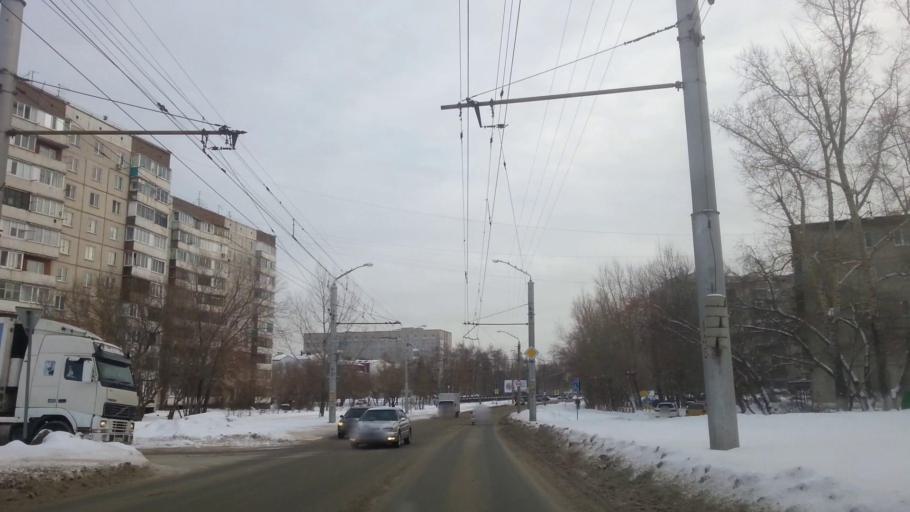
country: RU
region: Altai Krai
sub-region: Gorod Barnaulskiy
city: Barnaul
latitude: 53.3691
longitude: 83.7014
